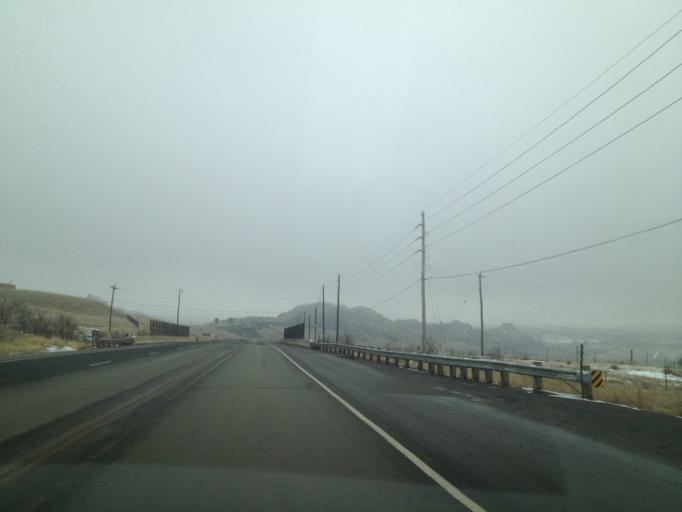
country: US
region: Colorado
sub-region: Jefferson County
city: Golden
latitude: 39.8601
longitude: -105.2355
